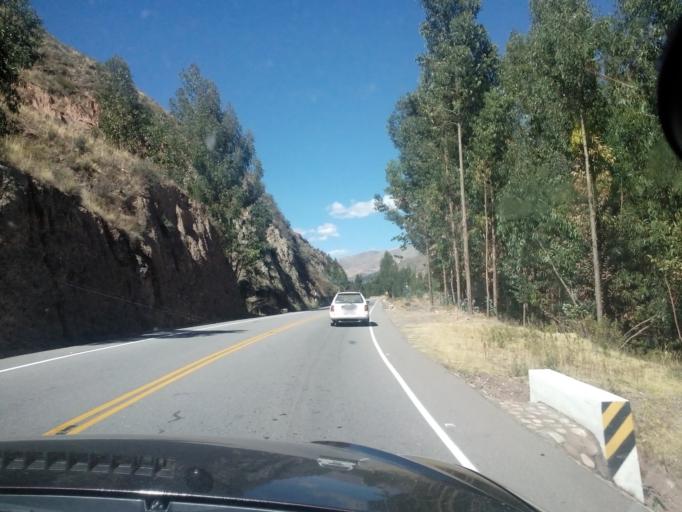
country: PE
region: Cusco
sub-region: Provincia de Canchis
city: Checacupe
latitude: -14.0353
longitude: -71.4501
